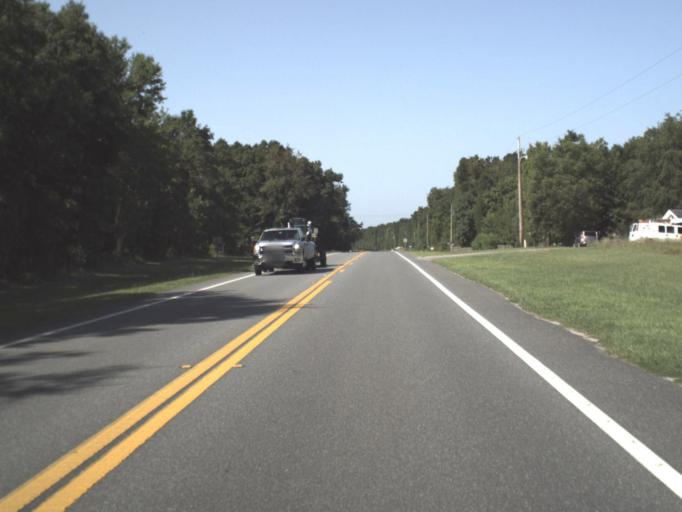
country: US
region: Florida
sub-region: Alachua County
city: High Springs
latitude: 29.9133
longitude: -82.7163
